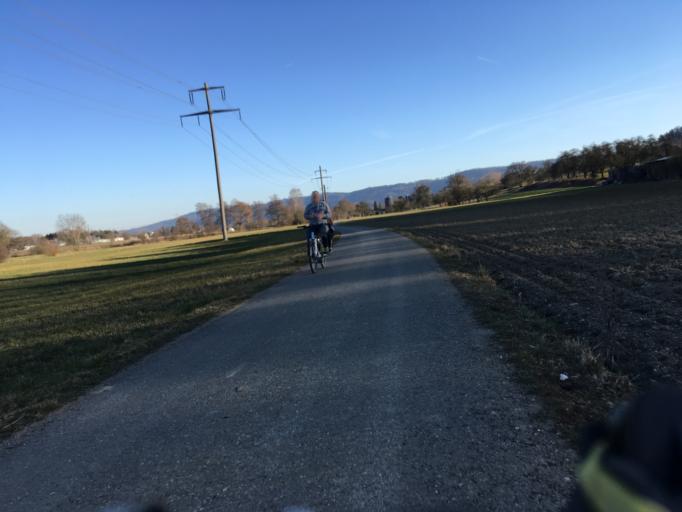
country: DE
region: Baden-Wuerttemberg
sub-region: Freiburg Region
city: Rielasingen-Worblingen
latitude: 47.7442
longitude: 8.8266
